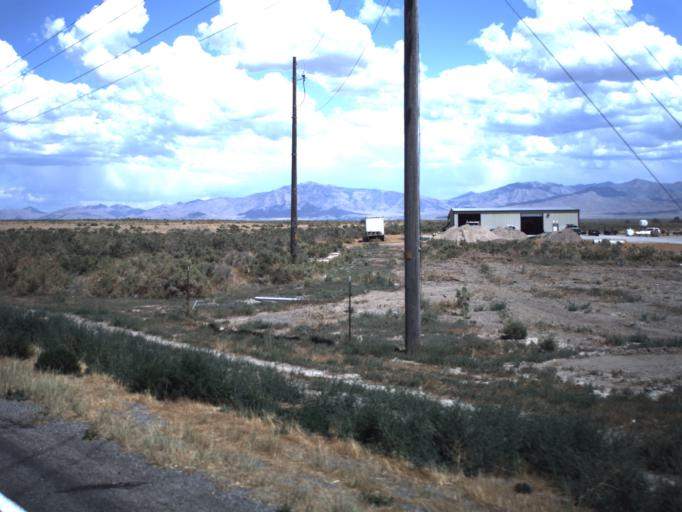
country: US
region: Utah
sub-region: Millard County
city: Delta
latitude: 39.3598
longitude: -112.5555
